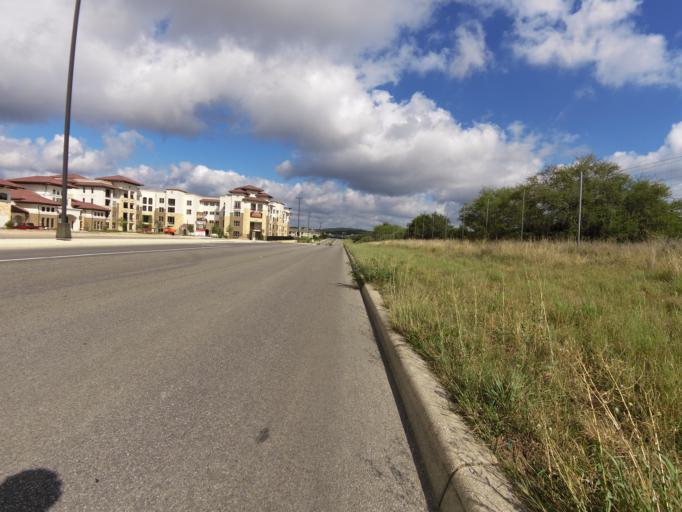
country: US
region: Texas
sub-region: Bexar County
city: Shavano Park
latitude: 29.5962
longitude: -98.5905
